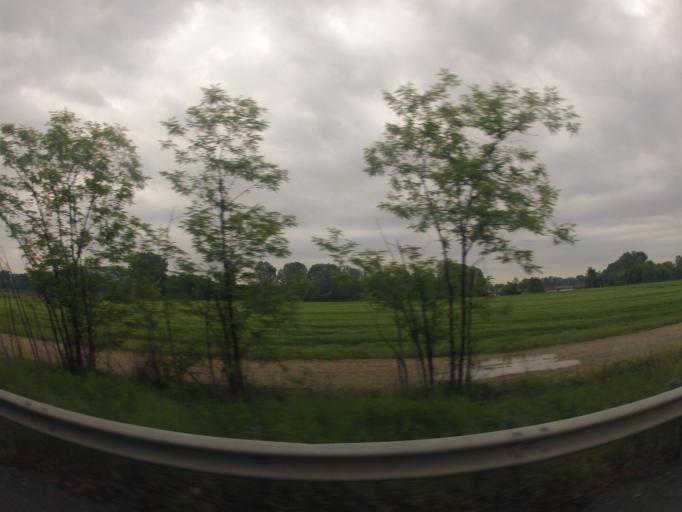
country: IT
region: Piedmont
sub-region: Provincia di Torino
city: La Loggia
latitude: 44.9620
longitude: 7.6788
